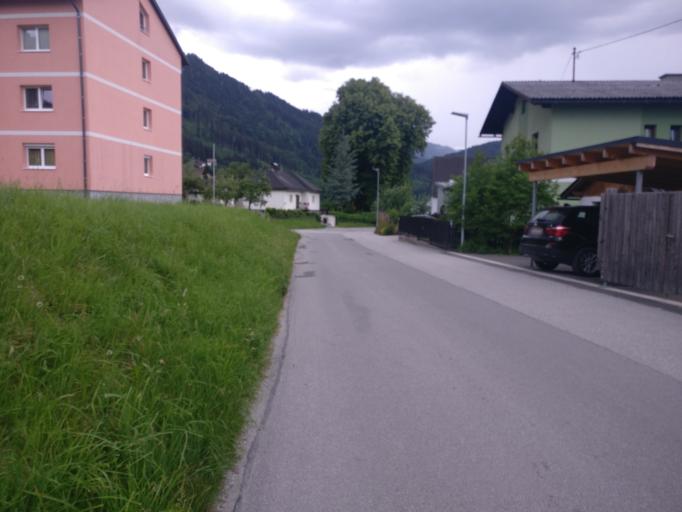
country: AT
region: Styria
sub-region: Politischer Bezirk Liezen
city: Selzthal
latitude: 47.5575
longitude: 14.3236
